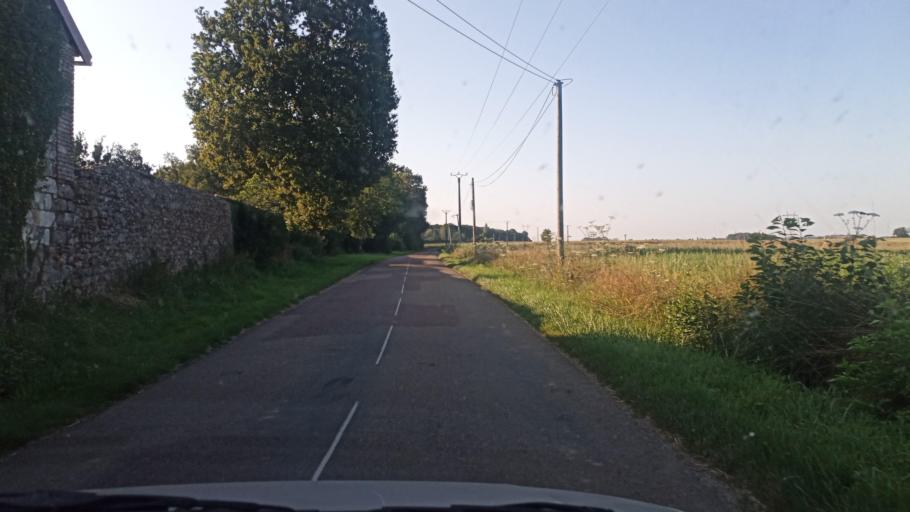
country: FR
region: Bourgogne
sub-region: Departement de l'Yonne
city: Saint-Valerien
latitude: 48.2251
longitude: 3.1191
